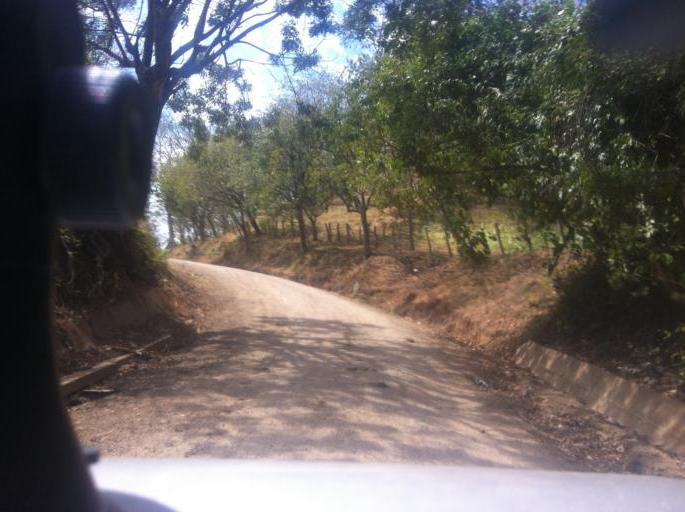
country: NI
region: Granada
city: Nandaime
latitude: 11.6323
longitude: -86.0146
